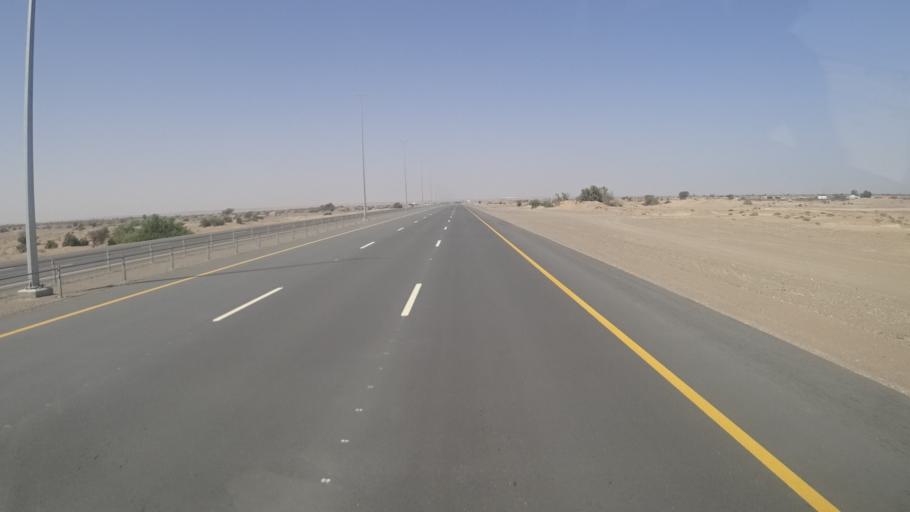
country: OM
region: Ash Sharqiyah
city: Badiyah
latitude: 22.2767
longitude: 59.1883
